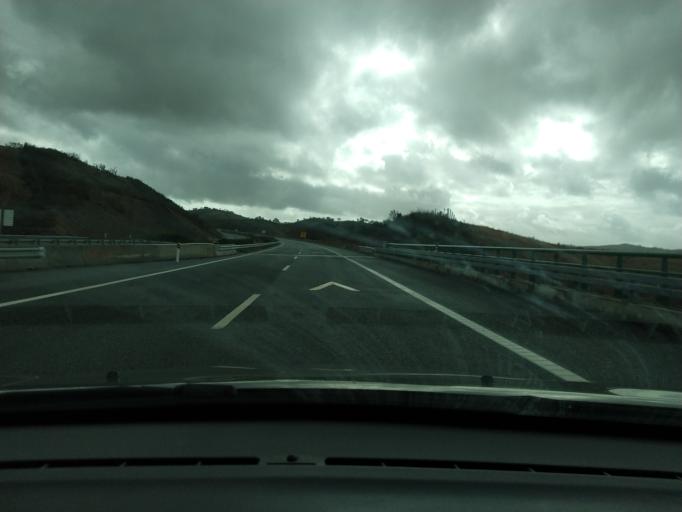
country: PT
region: Beja
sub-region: Almodovar
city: Almodovar
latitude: 37.4642
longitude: -8.2243
